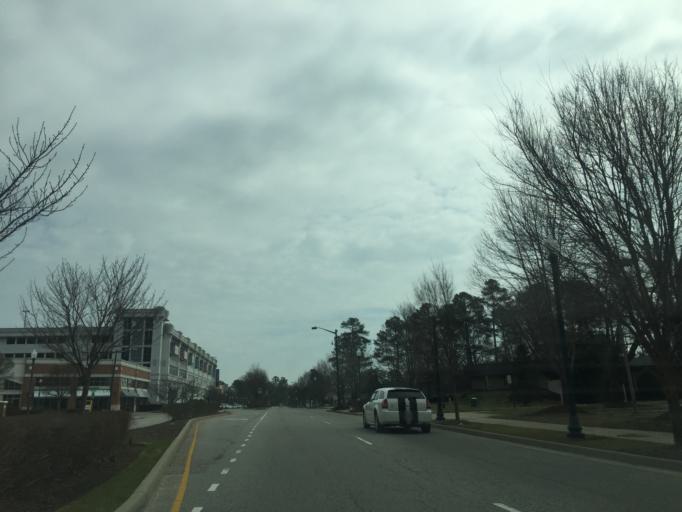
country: US
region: Virginia
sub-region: City of Newport News
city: Newport News
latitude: 37.0851
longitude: -76.4754
